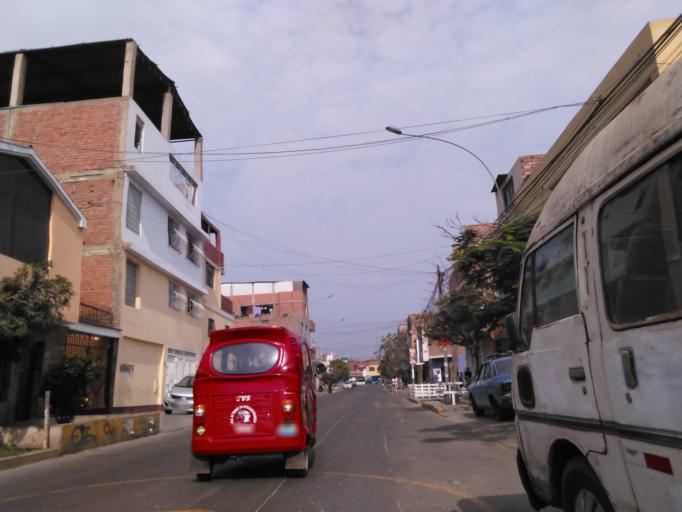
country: PE
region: Callao
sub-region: Callao
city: Callao
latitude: -12.0374
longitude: -77.0791
